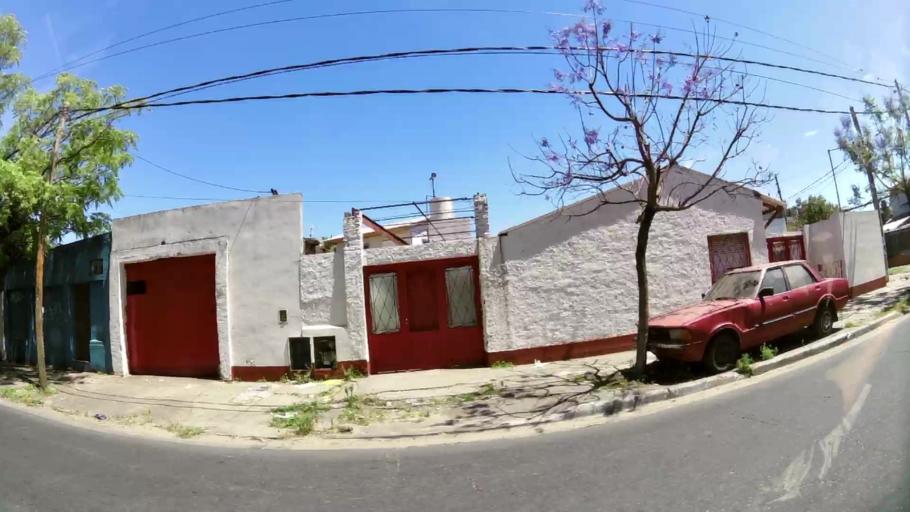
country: AR
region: Buenos Aires
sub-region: Partido de General San Martin
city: General San Martin
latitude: -34.5470
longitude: -58.5278
